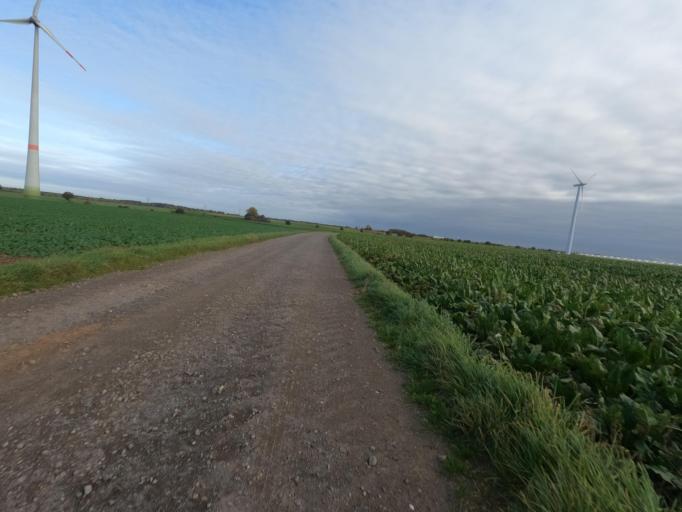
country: DE
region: North Rhine-Westphalia
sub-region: Regierungsbezirk Koln
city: Linnich
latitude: 51.0183
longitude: 6.2986
